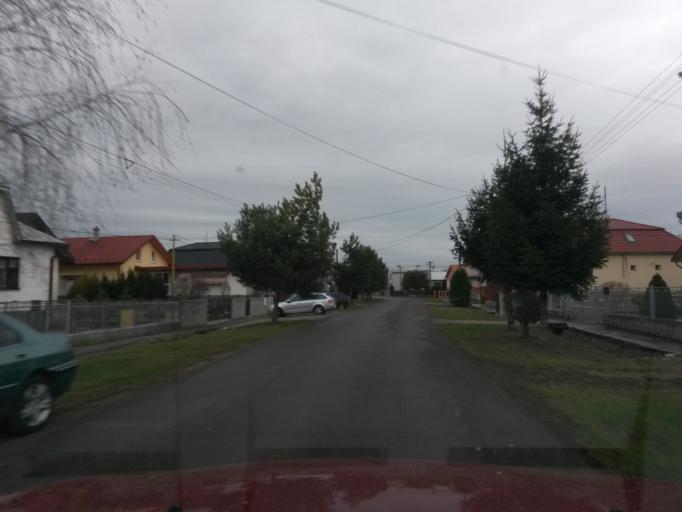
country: SK
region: Kosicky
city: Michalovce
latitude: 48.7021
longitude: 21.9224
